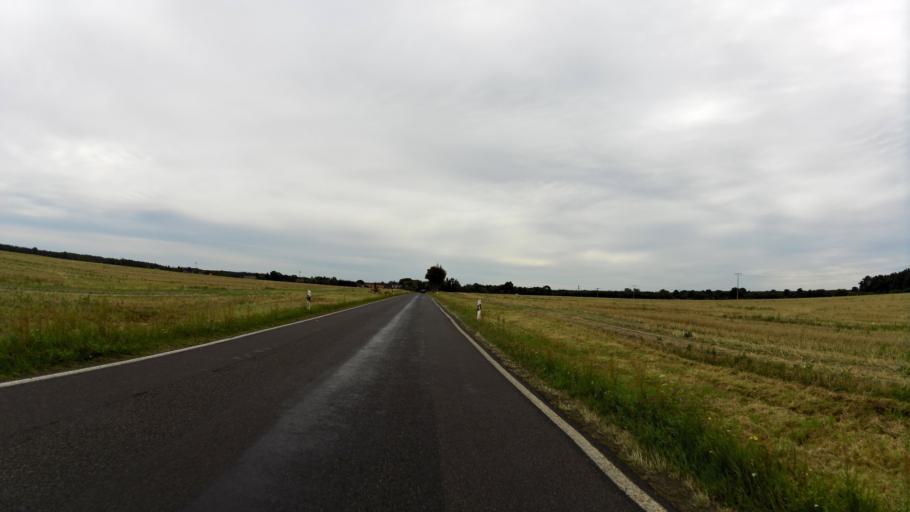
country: DE
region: Brandenburg
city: Wendisch Rietz
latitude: 52.1787
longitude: 14.0658
